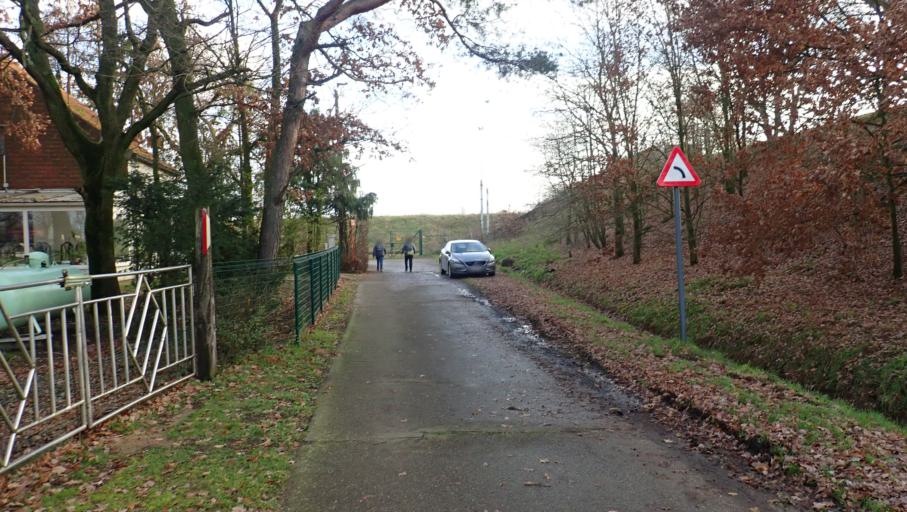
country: BE
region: Flanders
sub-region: Provincie Antwerpen
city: Brecht
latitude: 51.3696
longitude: 4.6464
